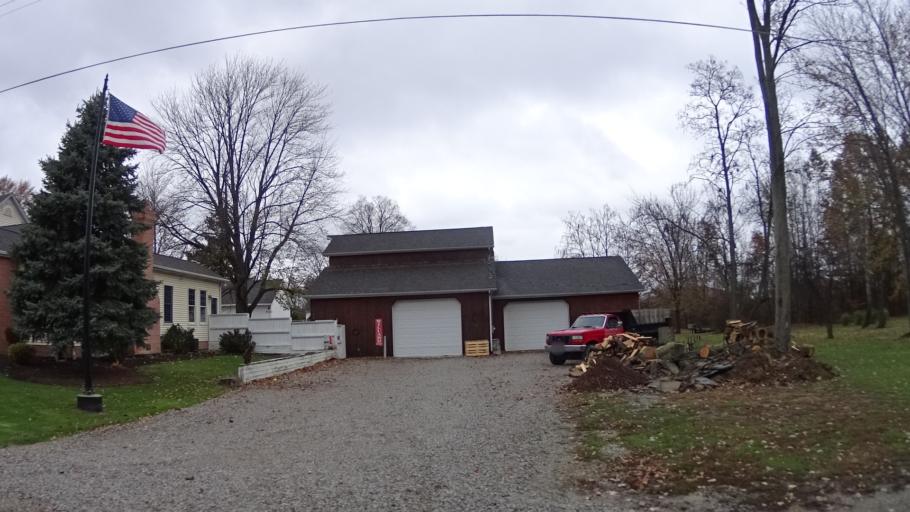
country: US
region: Ohio
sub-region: Lorain County
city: Elyria
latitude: 41.3976
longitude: -82.1297
